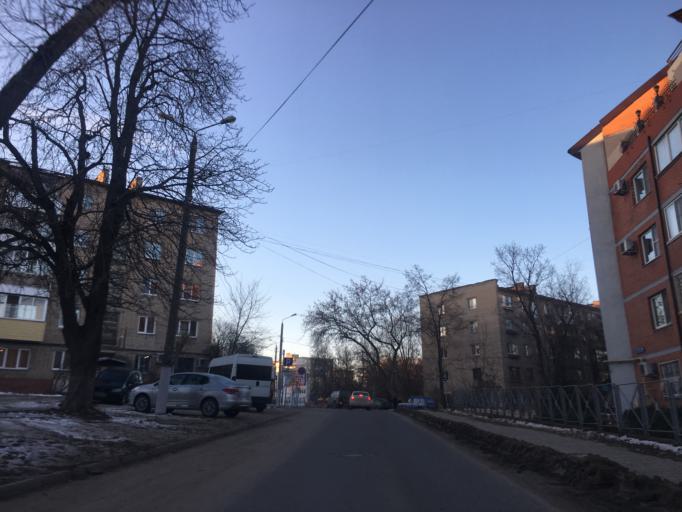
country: RU
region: Tula
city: Tula
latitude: 54.1889
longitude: 37.5936
